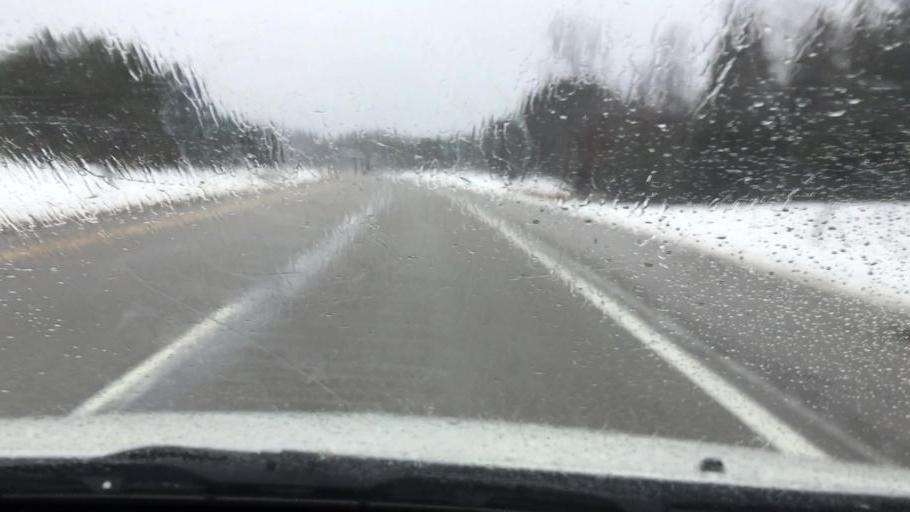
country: US
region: Michigan
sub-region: Wexford County
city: Cadillac
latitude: 44.1479
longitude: -85.4646
